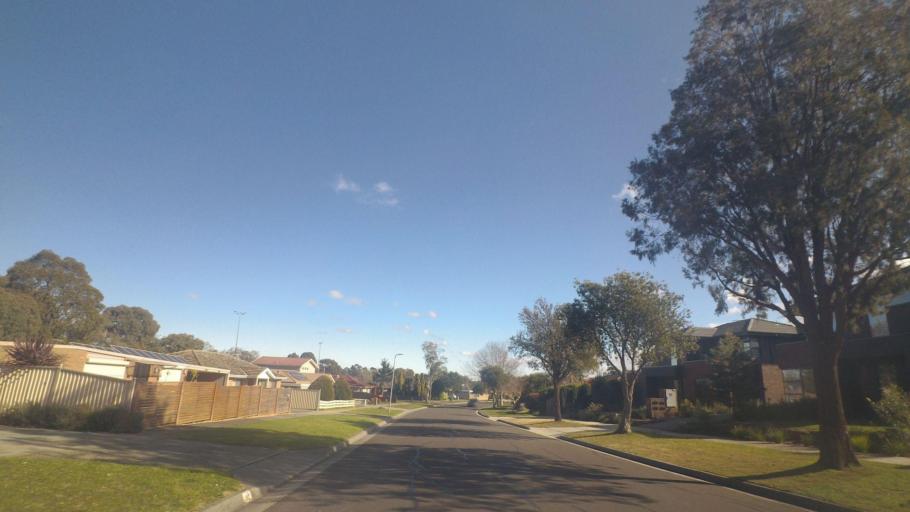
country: AU
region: Victoria
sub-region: Knox
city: Rowville
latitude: -37.9168
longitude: 145.2534
